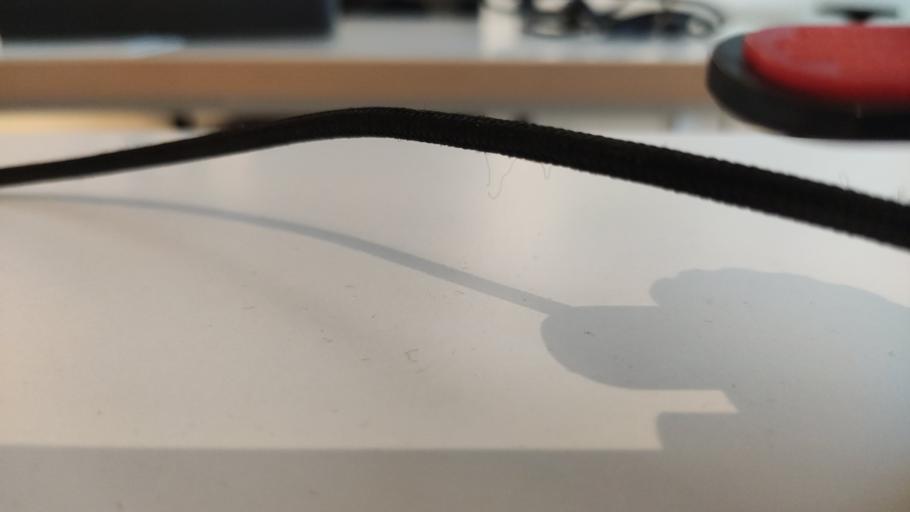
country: RU
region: Moskovskaya
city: Novopetrovskoye
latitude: 55.9424
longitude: 36.4361
